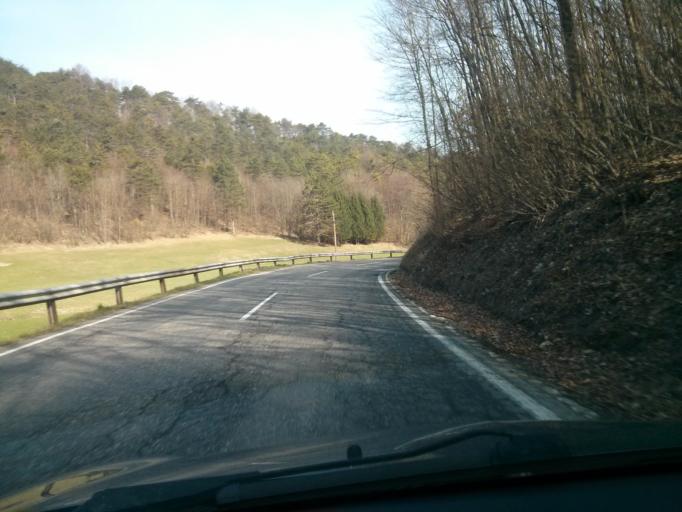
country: AT
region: Lower Austria
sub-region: Politischer Bezirk Baden
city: Hernstein
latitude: 47.9050
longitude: 16.0935
